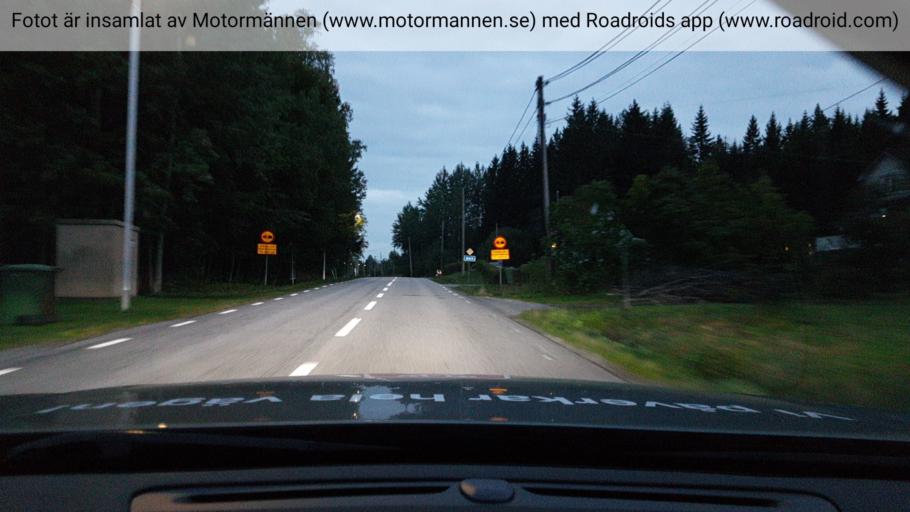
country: SE
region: OErebro
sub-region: Karlskoga Kommun
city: Karlskoga
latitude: 59.3716
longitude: 14.5713
